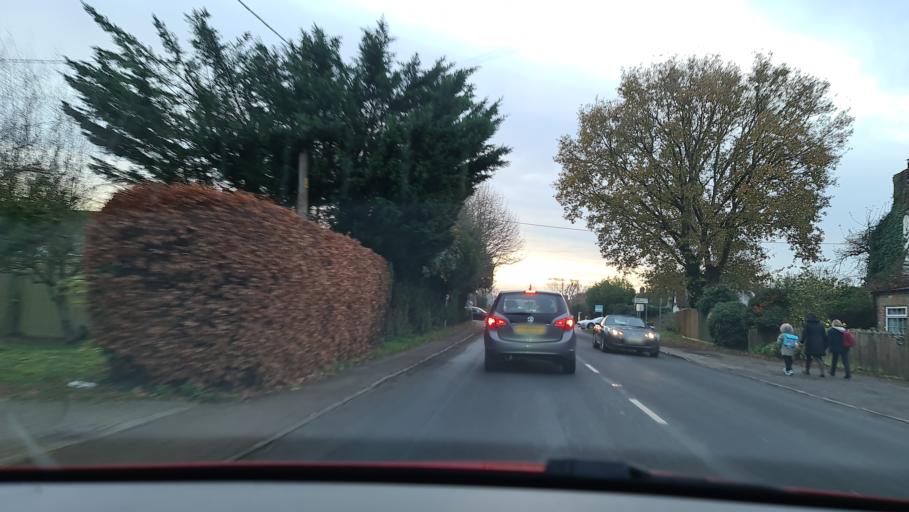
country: GB
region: England
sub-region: Buckinghamshire
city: Princes Risborough
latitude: 51.7394
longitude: -0.8612
